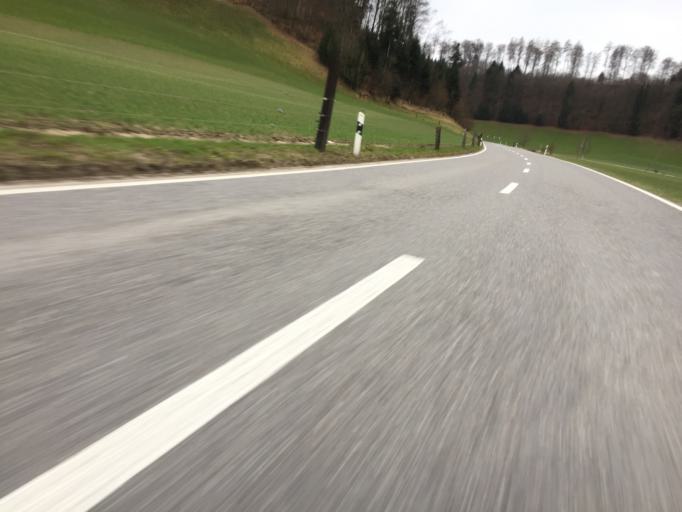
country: CH
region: Bern
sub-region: Emmental District
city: Krauchthal
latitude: 47.0205
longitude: 7.5720
